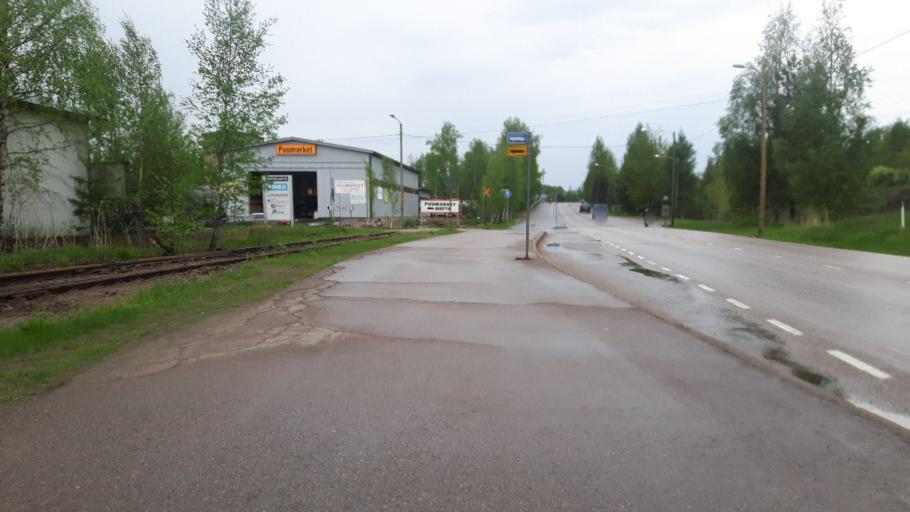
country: FI
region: Kymenlaakso
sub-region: Kotka-Hamina
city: Karhula
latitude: 60.5026
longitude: 26.9023
